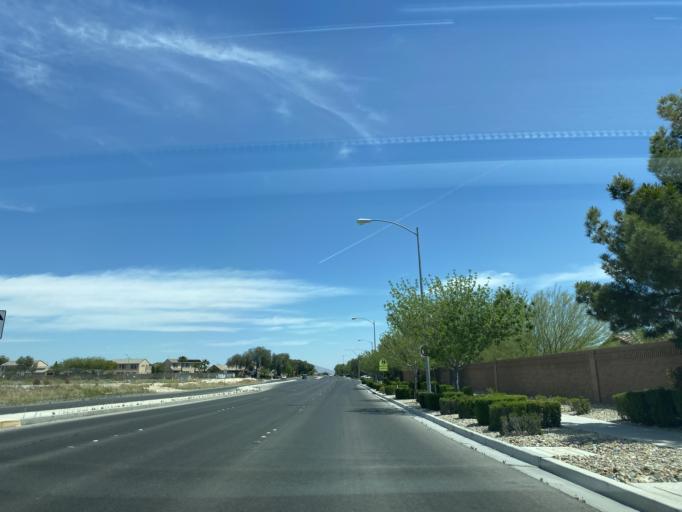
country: US
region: Nevada
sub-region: Clark County
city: Nellis Air Force Base
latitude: 36.2691
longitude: -115.0919
